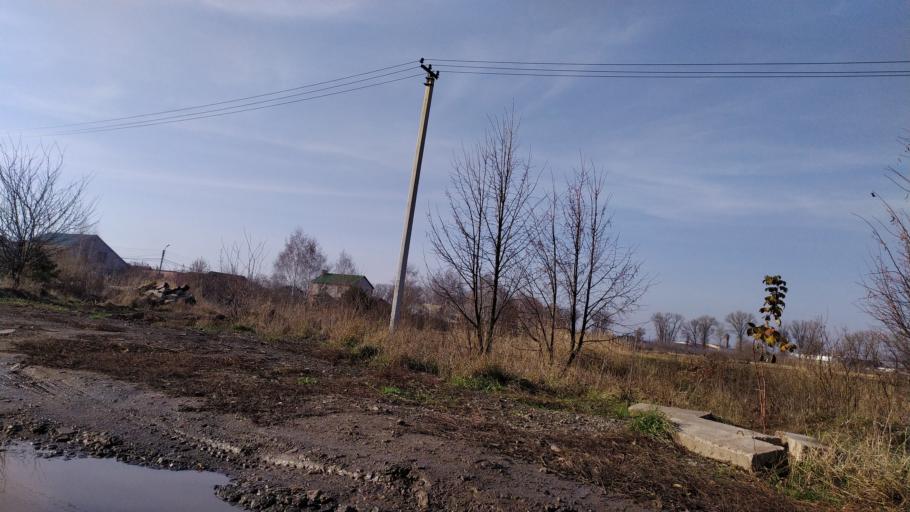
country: RU
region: Kursk
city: Voroshnevo
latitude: 51.6389
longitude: 36.1295
